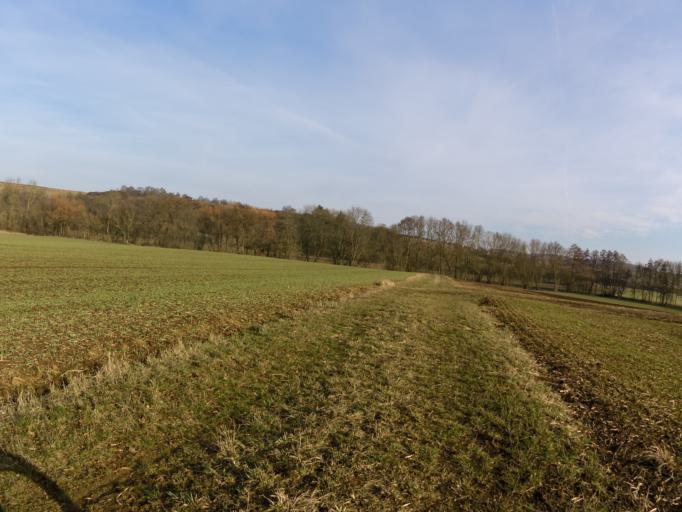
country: DE
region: Bavaria
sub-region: Regierungsbezirk Unterfranken
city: Estenfeld
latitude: 49.8386
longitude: 10.0198
